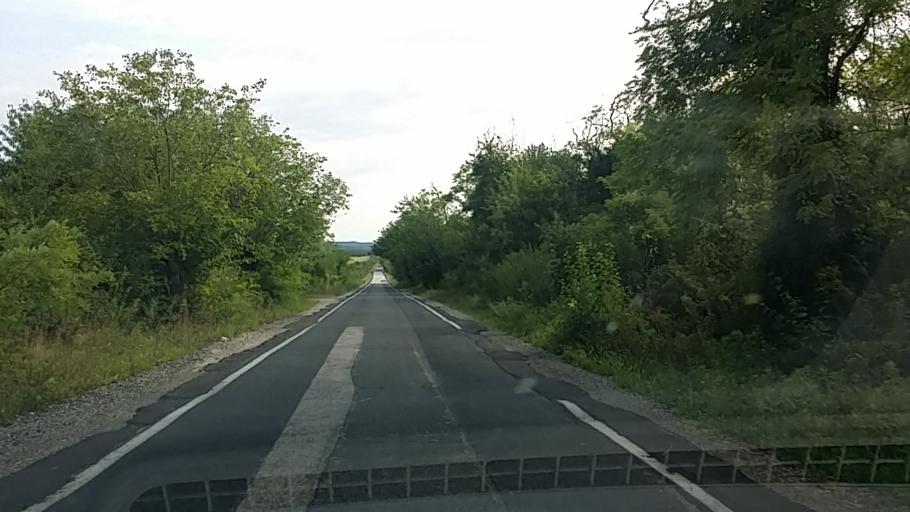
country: HU
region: Gyor-Moson-Sopron
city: Fertorakos
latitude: 47.7537
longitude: 16.6220
